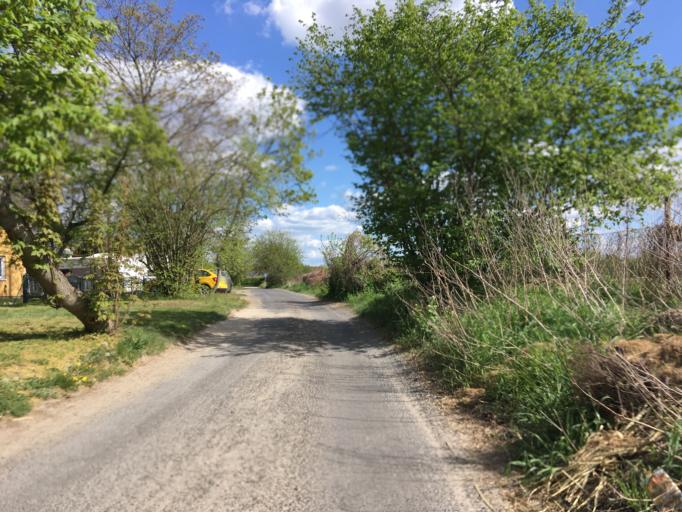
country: DE
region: Brandenburg
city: Hoppegarten
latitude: 52.5199
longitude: 13.6419
